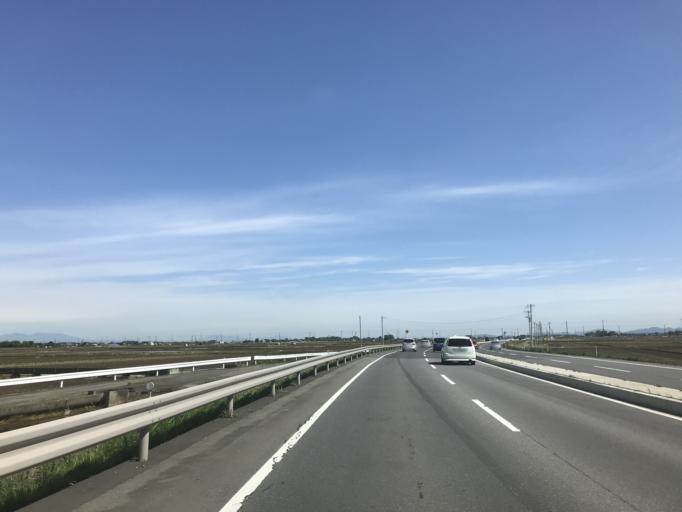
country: JP
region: Ibaraki
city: Ishige
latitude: 36.1275
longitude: 139.9820
